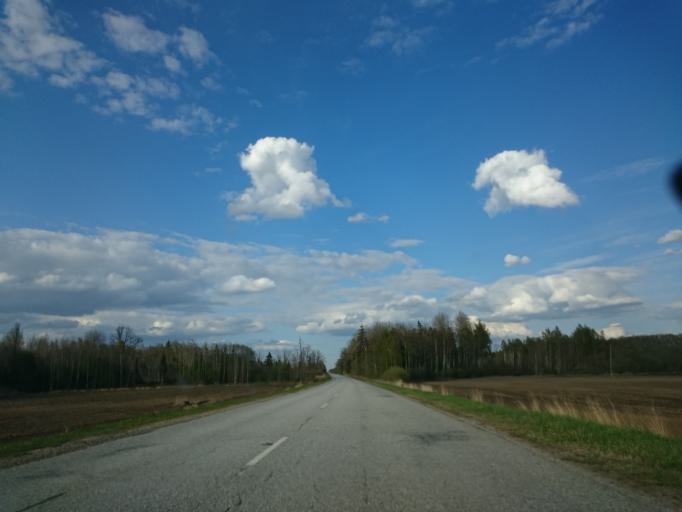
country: LV
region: Aizpute
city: Aizpute
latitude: 56.8097
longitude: 21.7111
